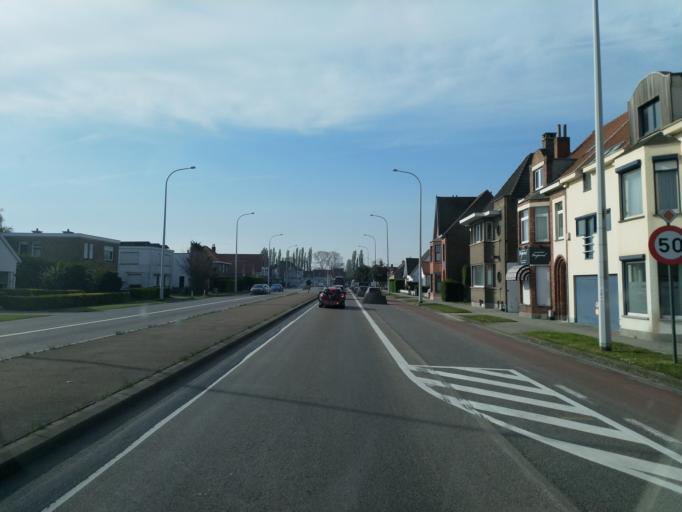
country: BE
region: Flanders
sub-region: Provincie West-Vlaanderen
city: Zeebrugge
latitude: 51.2964
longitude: 3.1918
